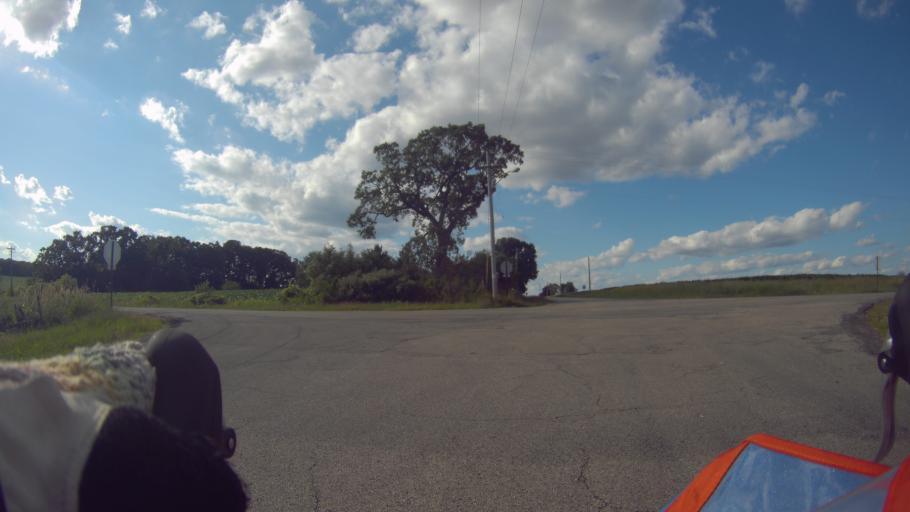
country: US
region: Wisconsin
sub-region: Dane County
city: McFarland
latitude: 42.9607
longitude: -89.3183
